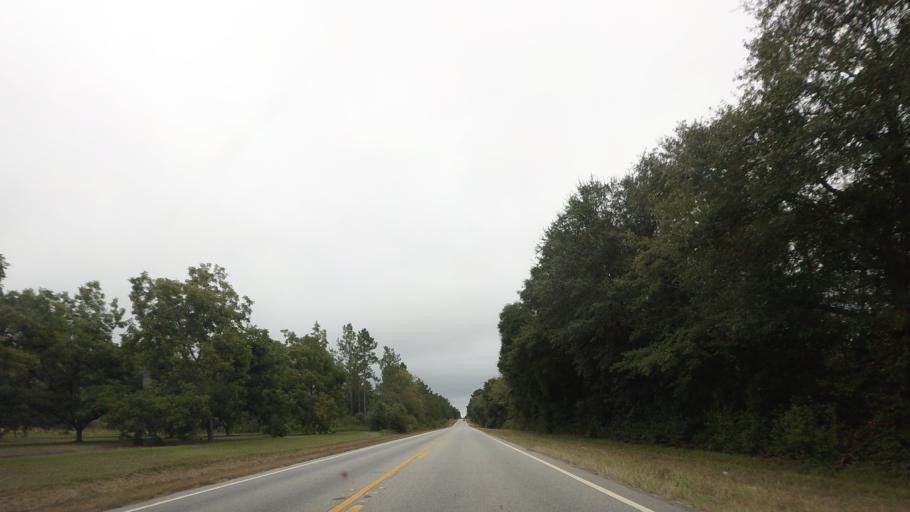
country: US
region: Georgia
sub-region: Berrien County
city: Ray City
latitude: 31.1047
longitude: -83.2089
